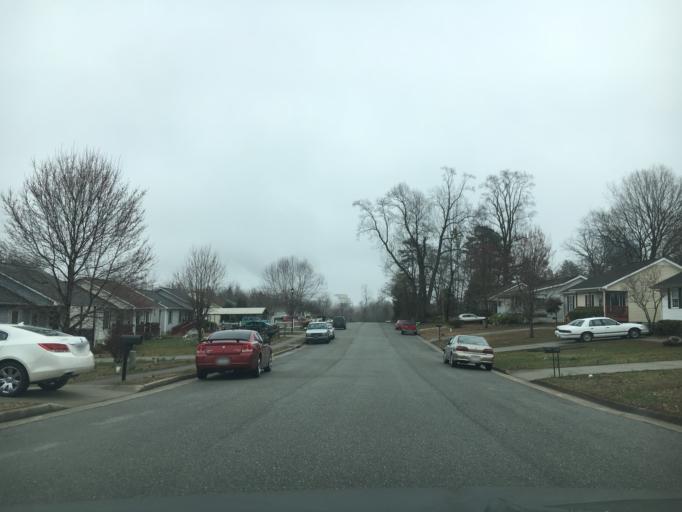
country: US
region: Virginia
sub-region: Halifax County
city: South Boston
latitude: 36.7007
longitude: -78.8856
